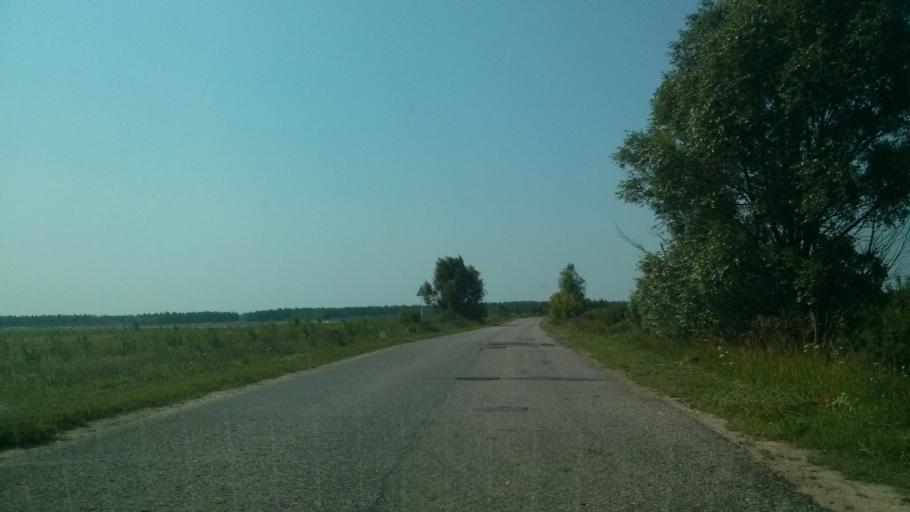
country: RU
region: Nizjnij Novgorod
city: Shimorskoye
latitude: 55.4348
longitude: 41.9740
